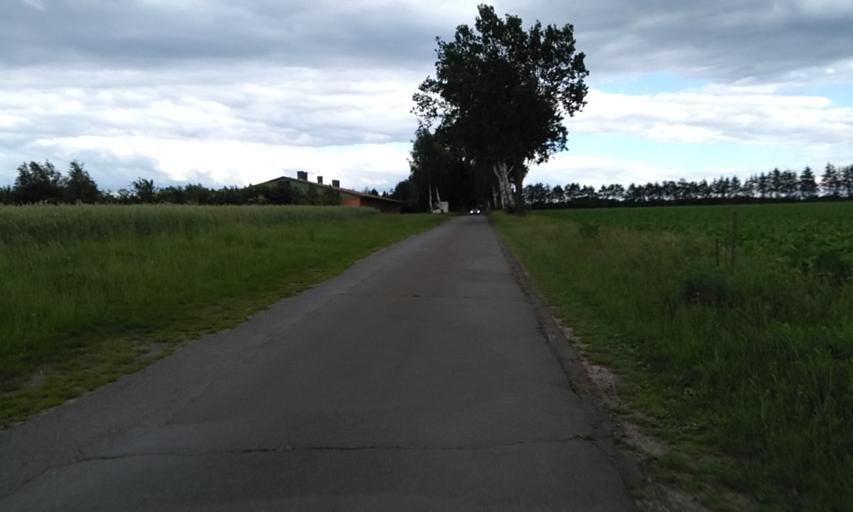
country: DE
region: Lower Saxony
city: Regesbostel
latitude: 53.3957
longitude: 9.6378
